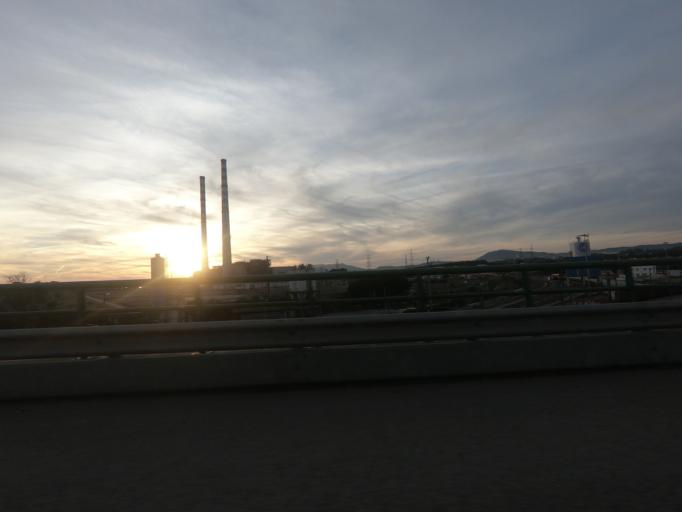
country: PT
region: Setubal
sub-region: Setubal
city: Setubal
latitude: 38.5129
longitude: -8.8386
